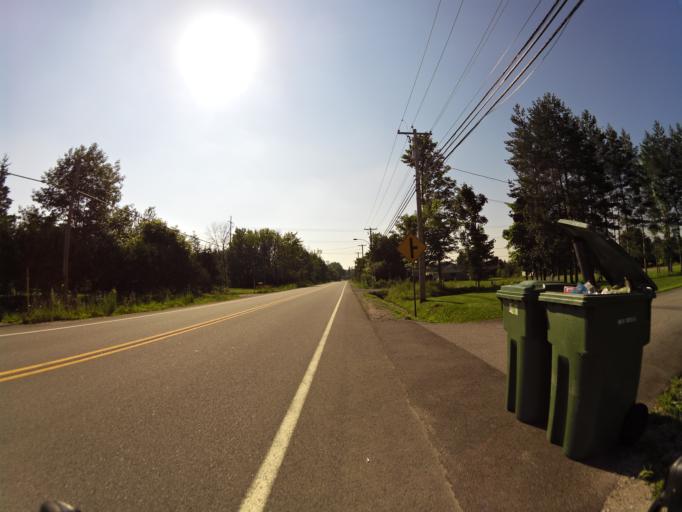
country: CA
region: Quebec
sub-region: Outaouais
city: Gatineau
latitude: 45.4939
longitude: -75.7725
